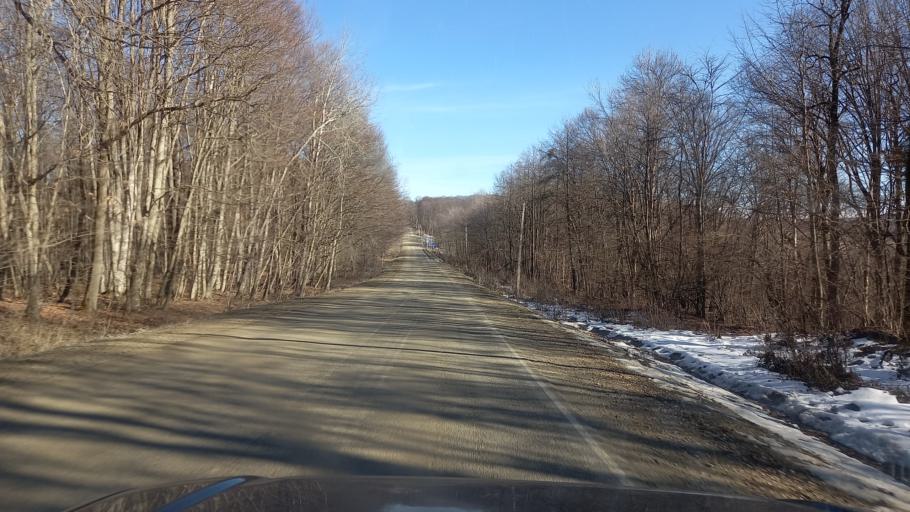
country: RU
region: Adygeya
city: Kamennomostskiy
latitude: 44.2780
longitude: 40.2852
